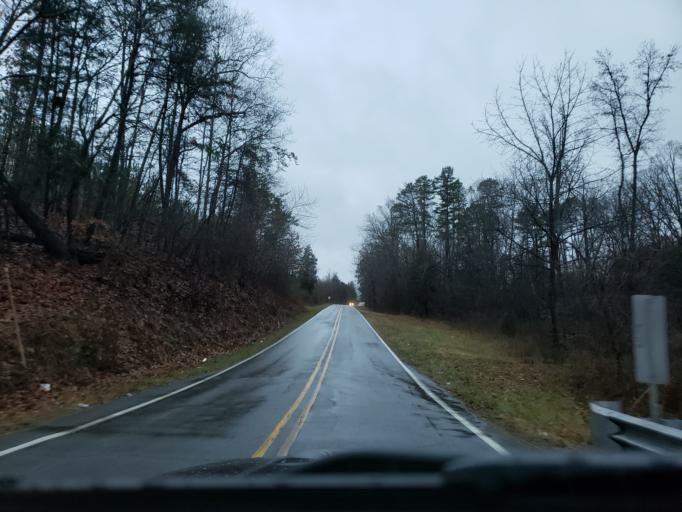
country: US
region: North Carolina
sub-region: Cleveland County
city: White Plains
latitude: 35.1890
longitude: -81.3829
